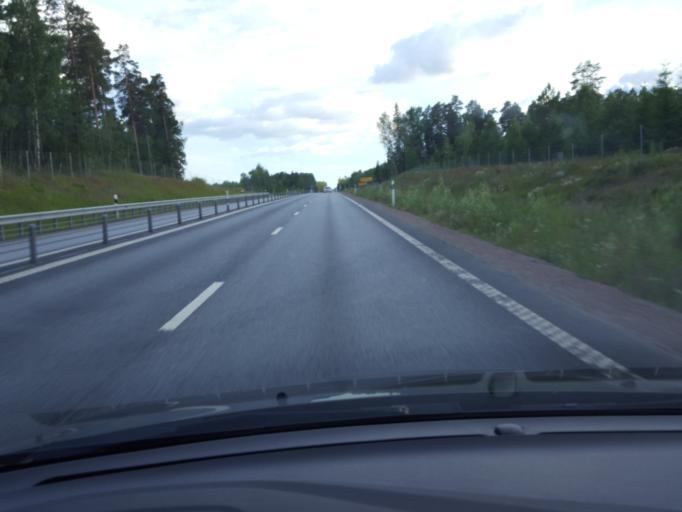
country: SE
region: Uppsala
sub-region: Osthammars Kommun
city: Osterbybruk
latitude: 59.9950
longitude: 17.9550
